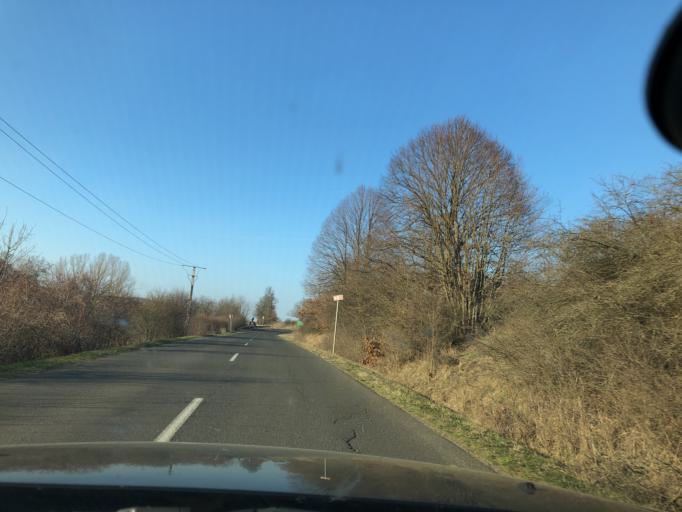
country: HU
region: Nograd
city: Rimoc
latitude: 47.9880
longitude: 19.6142
